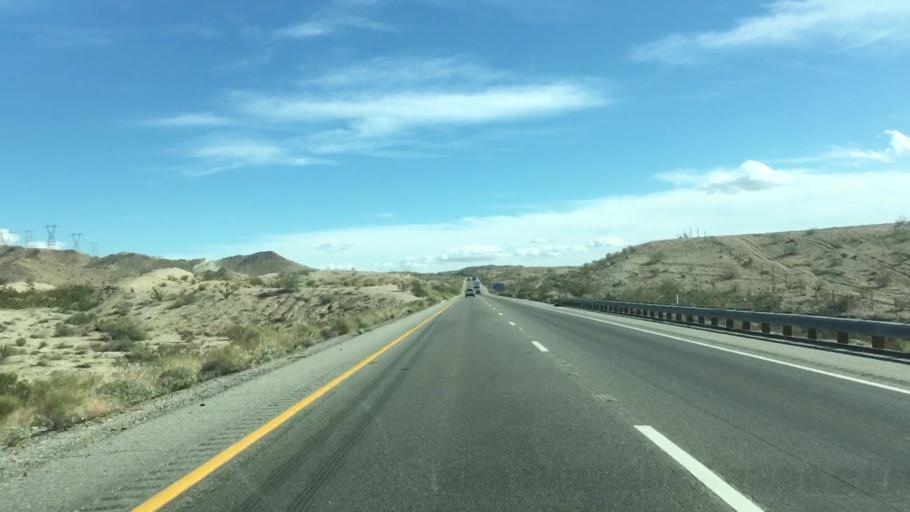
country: US
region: California
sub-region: Riverside County
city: Mecca
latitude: 33.6815
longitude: -116.0070
